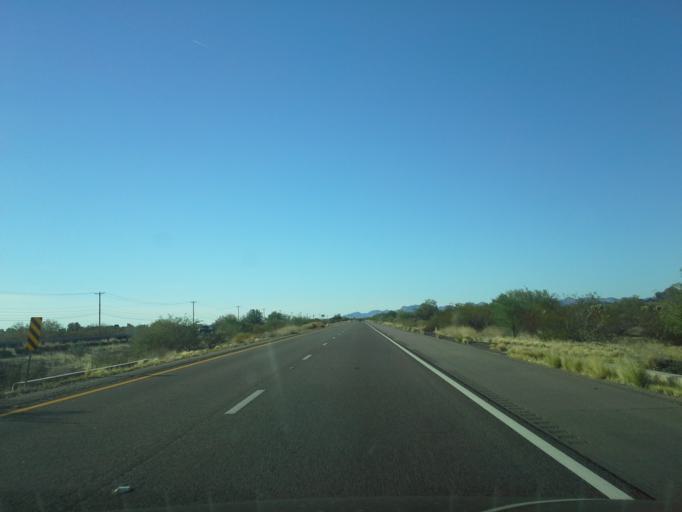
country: US
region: Arizona
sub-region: Pinal County
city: Gold Camp
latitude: 33.3159
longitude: -111.4172
